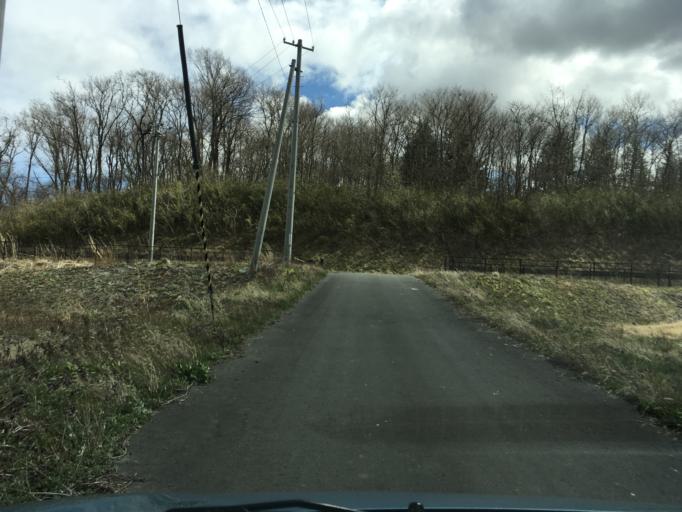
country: JP
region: Miyagi
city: Kogota
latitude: 38.6866
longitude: 141.0975
